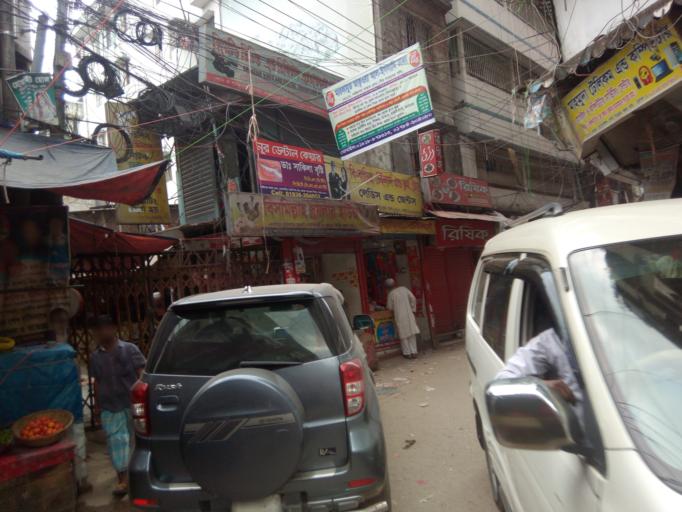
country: BD
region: Dhaka
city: Paltan
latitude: 23.7401
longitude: 90.4113
